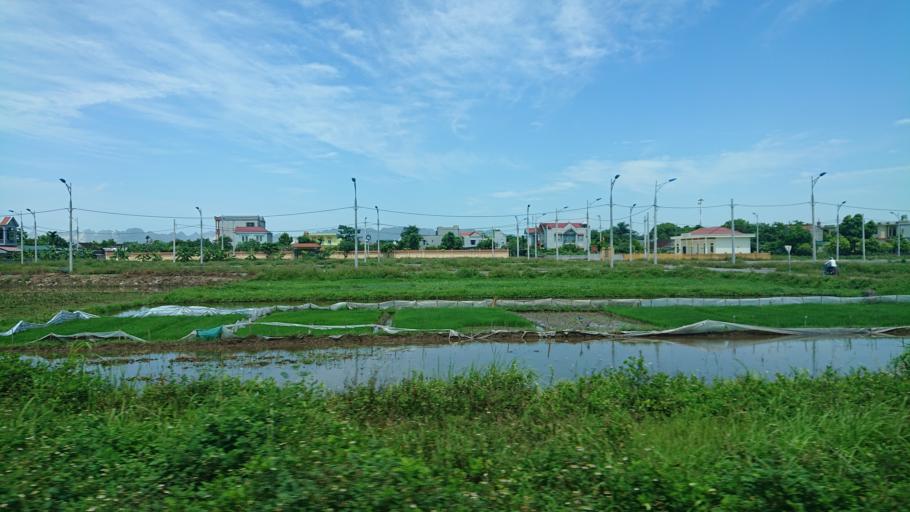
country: VN
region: Ha Nam
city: Thanh Pho Phu Ly
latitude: 20.5299
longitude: 105.9459
